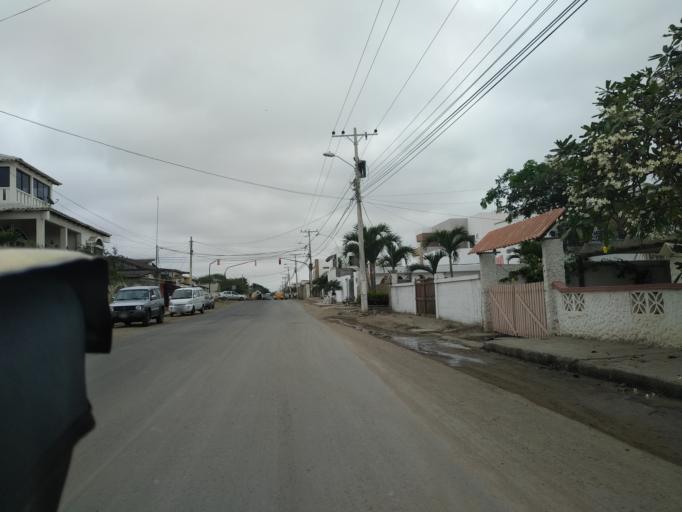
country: EC
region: Santa Elena
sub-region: Canton Santa Elena
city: Santa Elena
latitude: -2.2050
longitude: -80.8739
